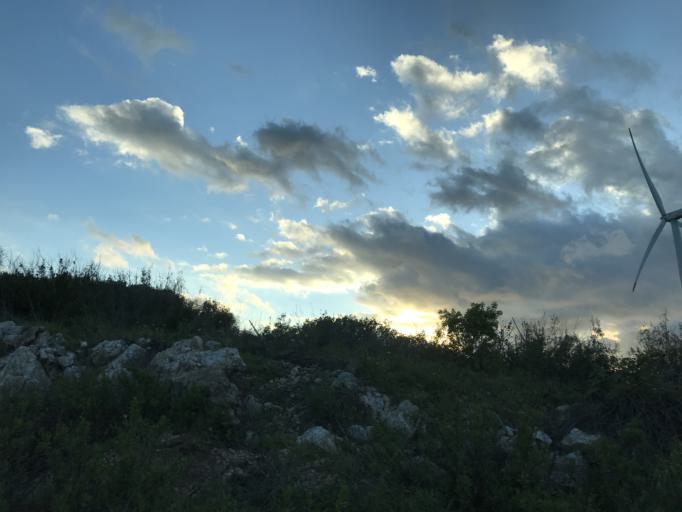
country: TR
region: Hatay
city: Buyukcat
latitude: 36.0951
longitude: 36.0377
